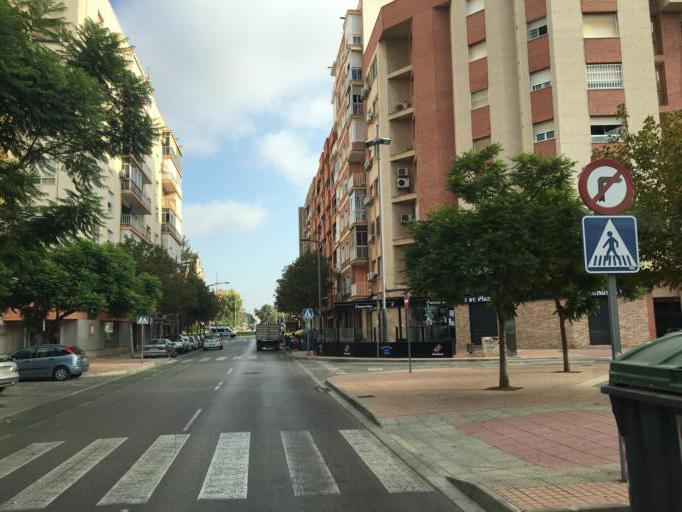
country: ES
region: Murcia
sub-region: Murcia
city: Cartagena
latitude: 37.6142
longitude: -0.9890
